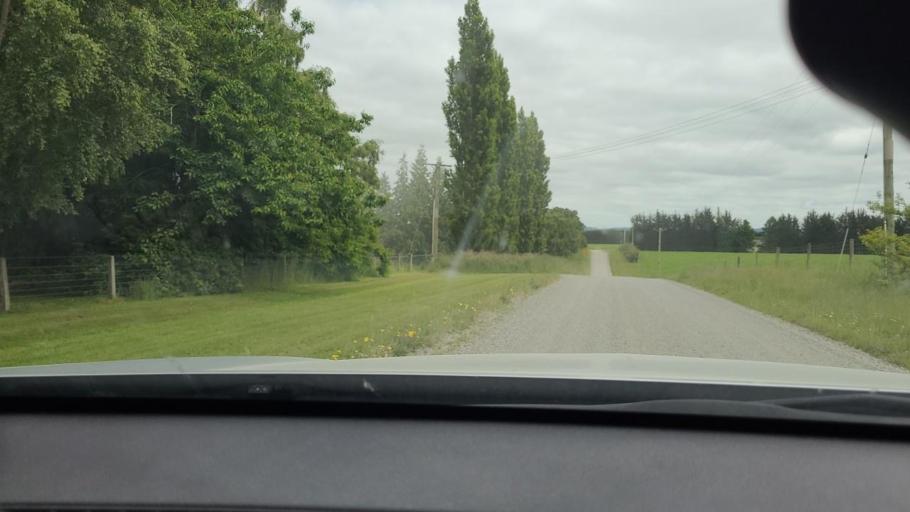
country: NZ
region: Southland
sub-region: Southland District
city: Riverton
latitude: -46.0657
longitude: 168.0148
